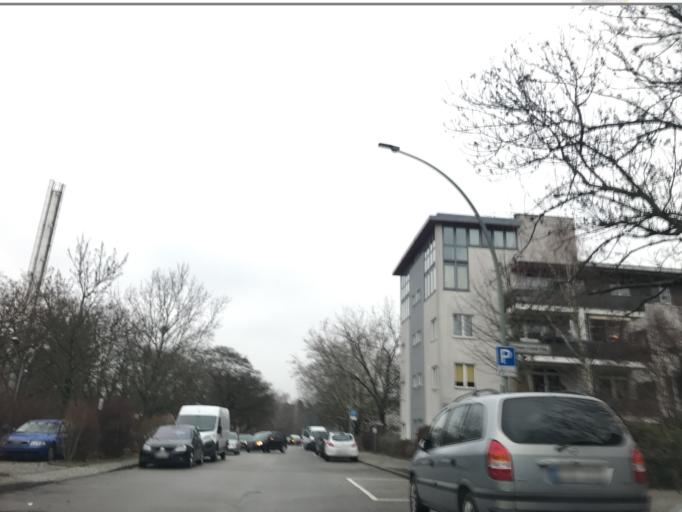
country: DE
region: Berlin
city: Falkenhagener Feld
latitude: 52.5512
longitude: 13.1727
